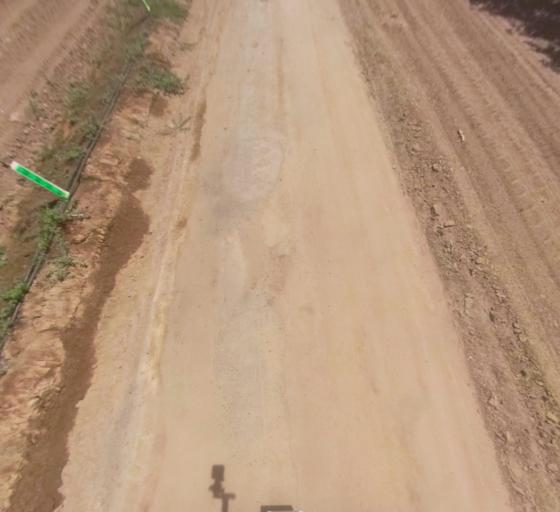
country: US
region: California
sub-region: Madera County
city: Bonadelle Ranchos-Madera Ranchos
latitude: 36.9165
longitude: -119.8953
